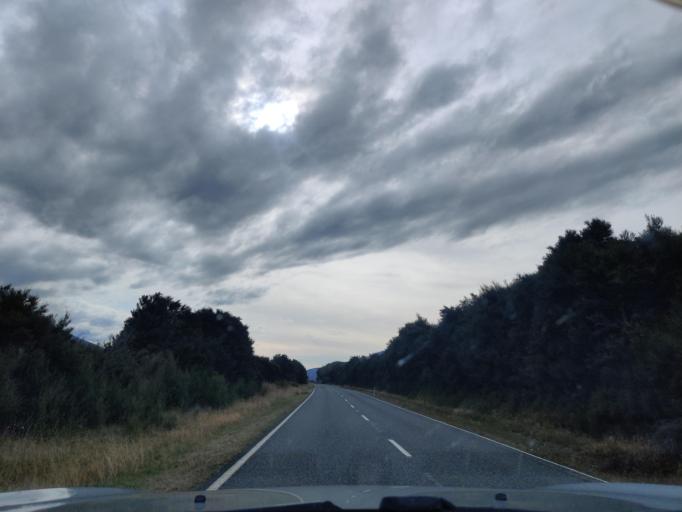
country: NZ
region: Tasman
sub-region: Tasman District
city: Wakefield
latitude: -41.7395
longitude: 173.0156
